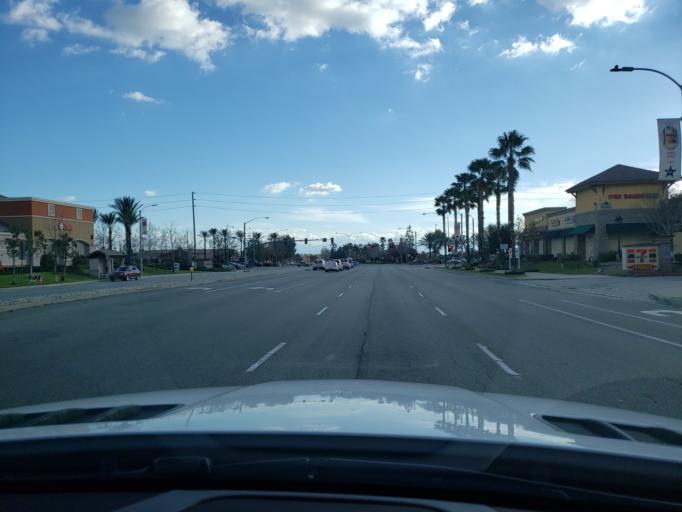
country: US
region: California
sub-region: San Bernardino County
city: Rancho Cucamonga
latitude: 34.0786
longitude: -117.5584
